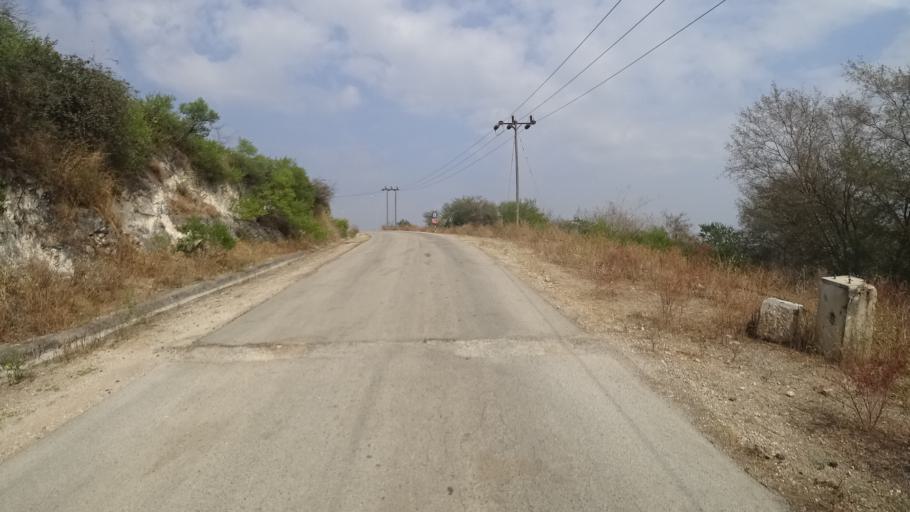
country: YE
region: Al Mahrah
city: Hawf
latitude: 16.7262
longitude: 53.2750
